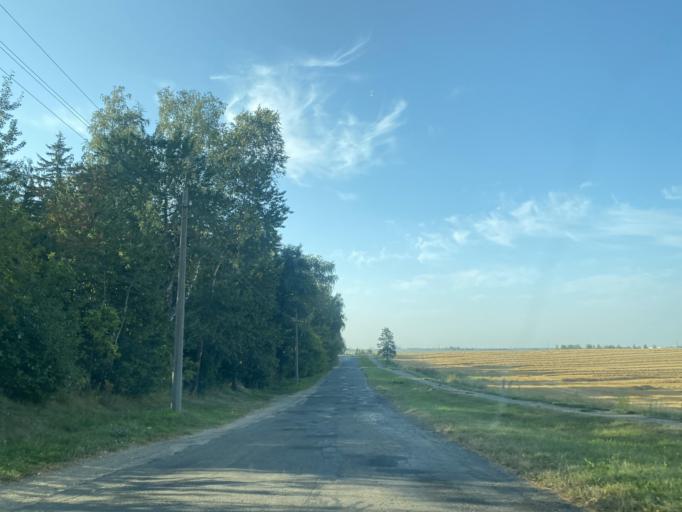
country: BY
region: Minsk
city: Hatava
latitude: 53.8316
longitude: 27.6386
